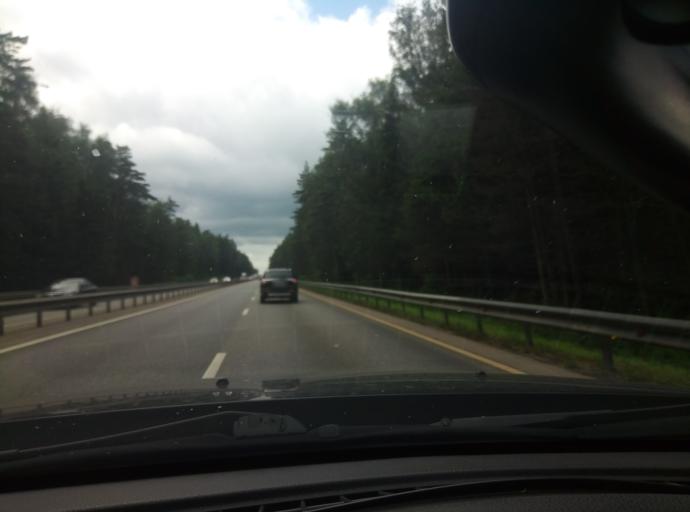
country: RU
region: Kaluga
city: Obninsk
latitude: 55.0250
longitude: 36.5684
